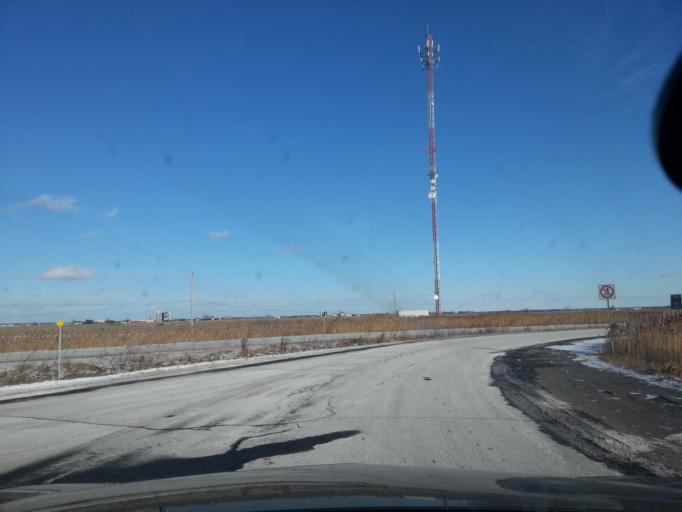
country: CA
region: Ontario
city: Casselman
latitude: 45.3276
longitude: -74.9851
